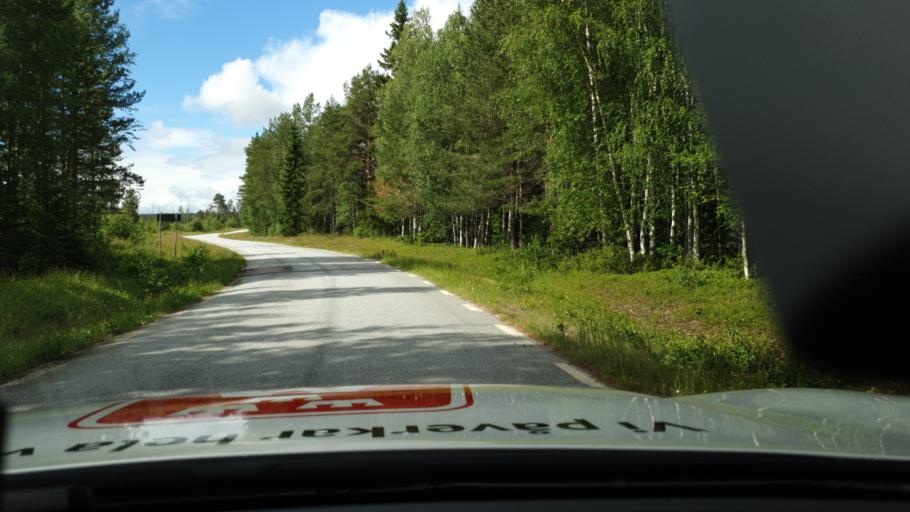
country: SE
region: Norrbotten
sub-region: Pitea Kommun
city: Rosvik
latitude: 65.4452
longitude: 21.9004
